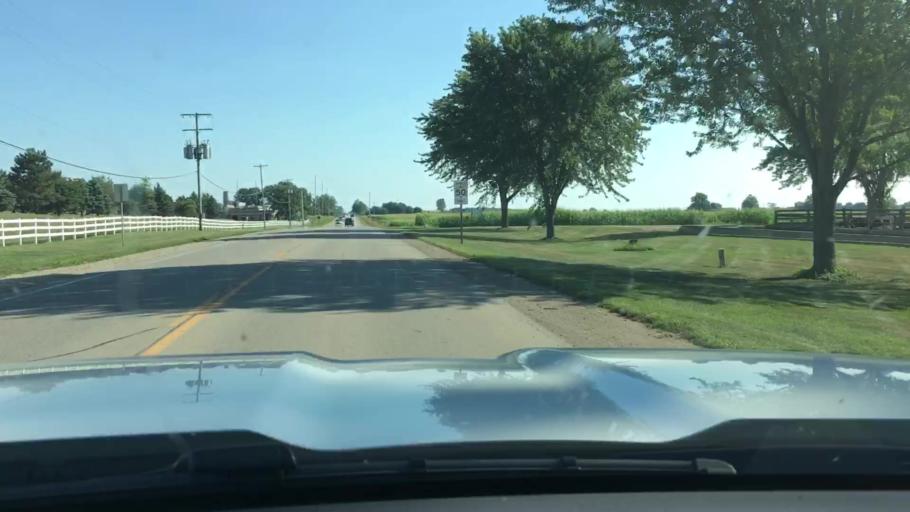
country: US
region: Michigan
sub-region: Ottawa County
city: Coopersville
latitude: 43.0514
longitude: -85.9568
